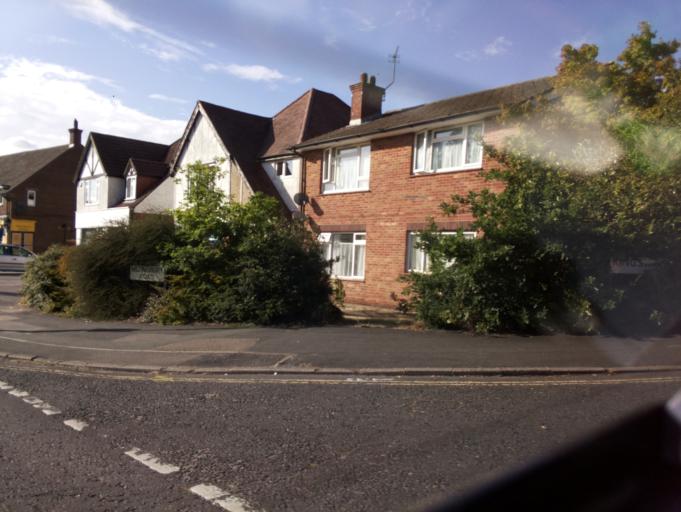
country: GB
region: England
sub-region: Hampshire
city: Chandlers Ford
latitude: 50.9956
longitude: -1.3693
